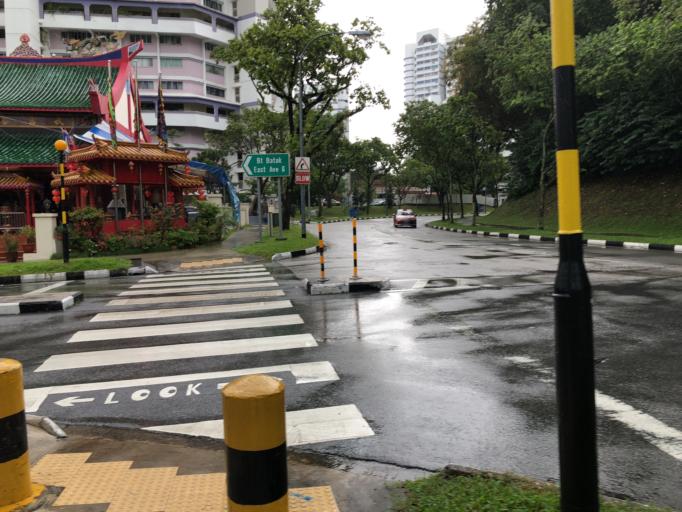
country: SG
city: Singapore
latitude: 1.3465
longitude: 103.7514
